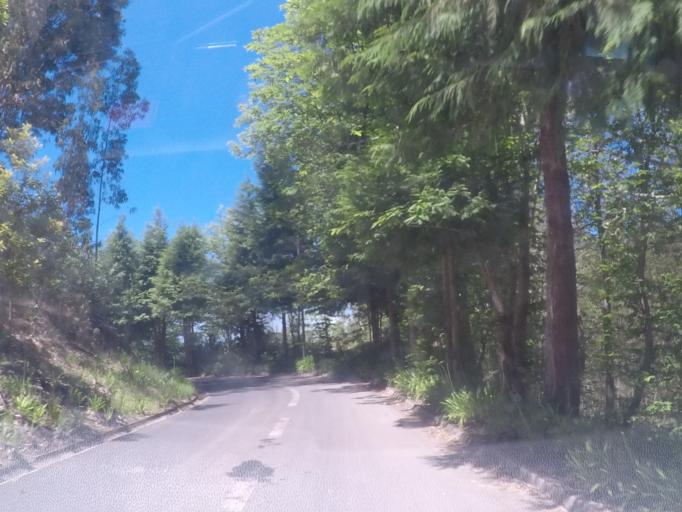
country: PT
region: Madeira
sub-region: Camara de Lobos
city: Curral das Freiras
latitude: 32.6944
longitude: -16.9781
